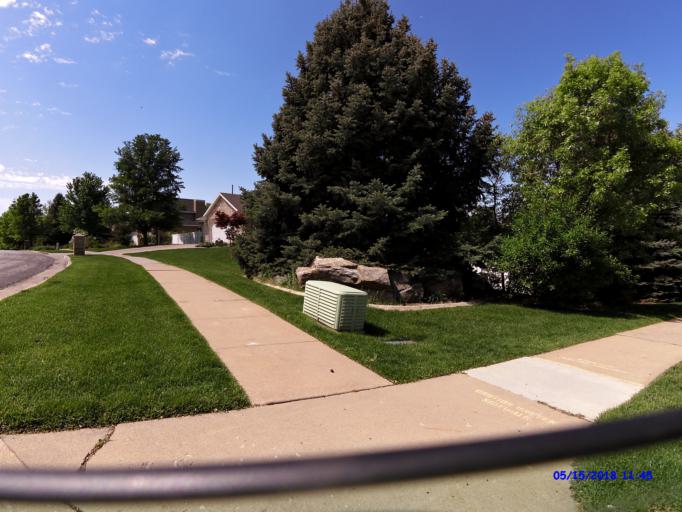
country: US
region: Utah
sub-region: Weber County
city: South Ogden
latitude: 41.1791
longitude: -111.9389
